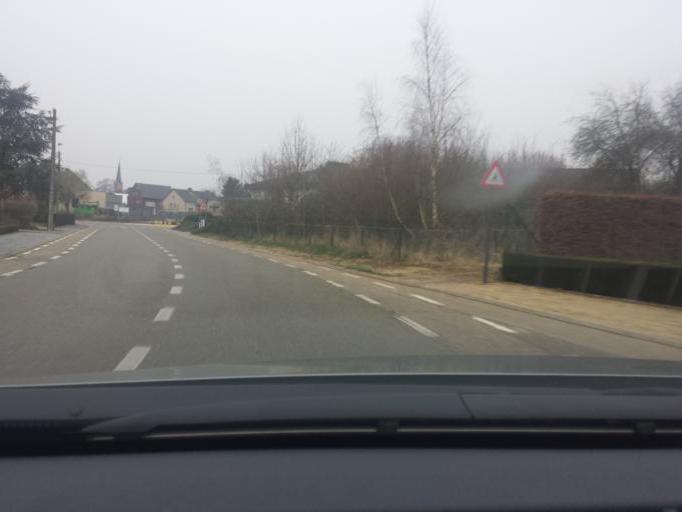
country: BE
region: Flanders
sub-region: Provincie Limburg
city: Beringen
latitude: 51.0449
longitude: 5.1693
